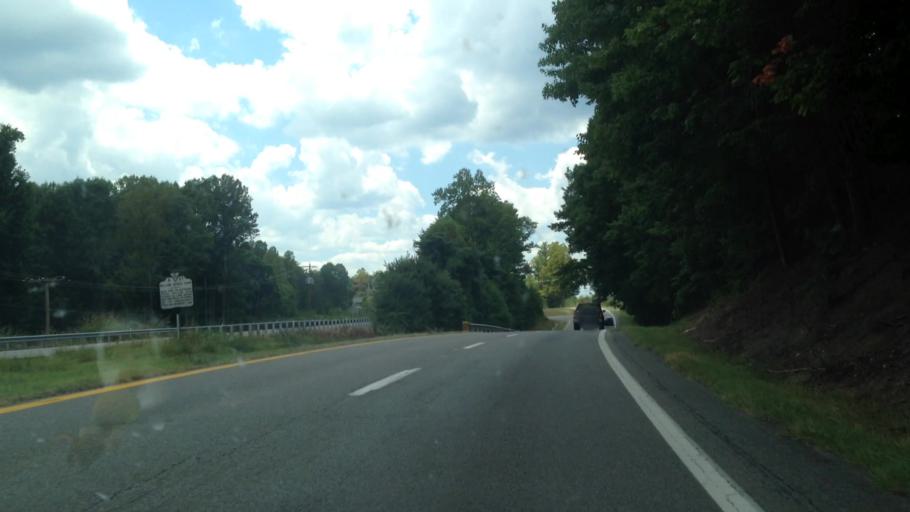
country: US
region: North Carolina
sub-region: Rockingham County
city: Stoneville
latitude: 36.5464
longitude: -79.9028
